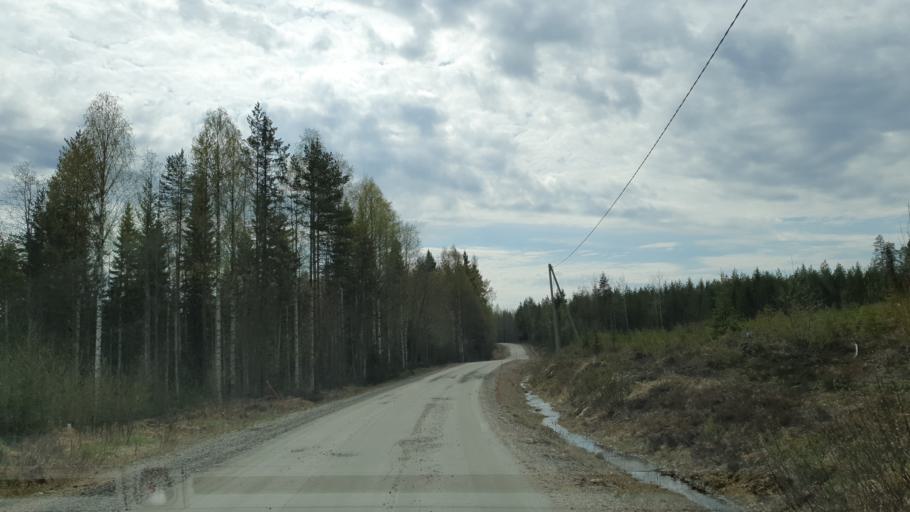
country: FI
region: Kainuu
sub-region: Kehys-Kainuu
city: Kuhmo
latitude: 64.1026
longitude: 29.9428
